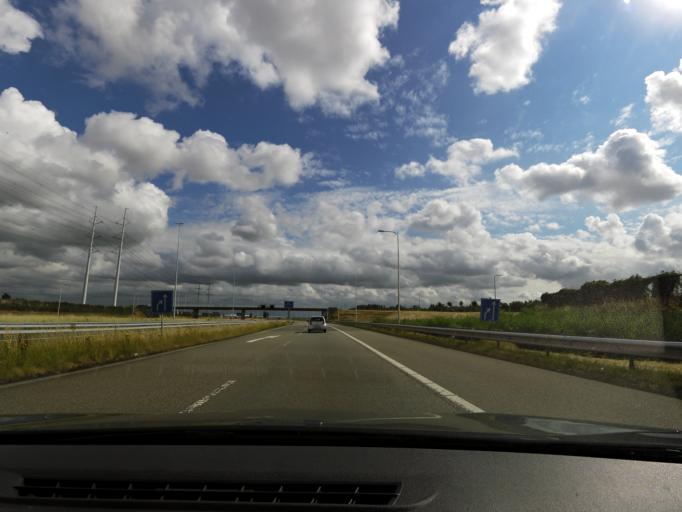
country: NL
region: South Holland
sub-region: Gemeente Rijswijk
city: Rijswijk
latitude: 52.0072
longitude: 4.3101
